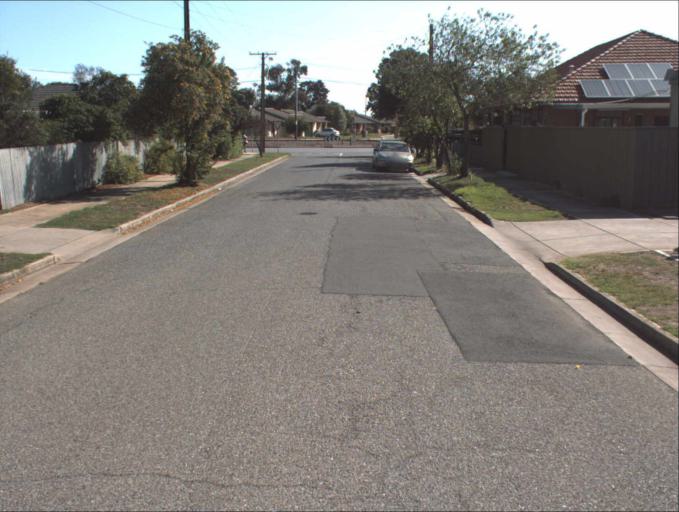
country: AU
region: South Australia
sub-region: Port Adelaide Enfield
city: Alberton
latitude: -34.8465
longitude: 138.5346
